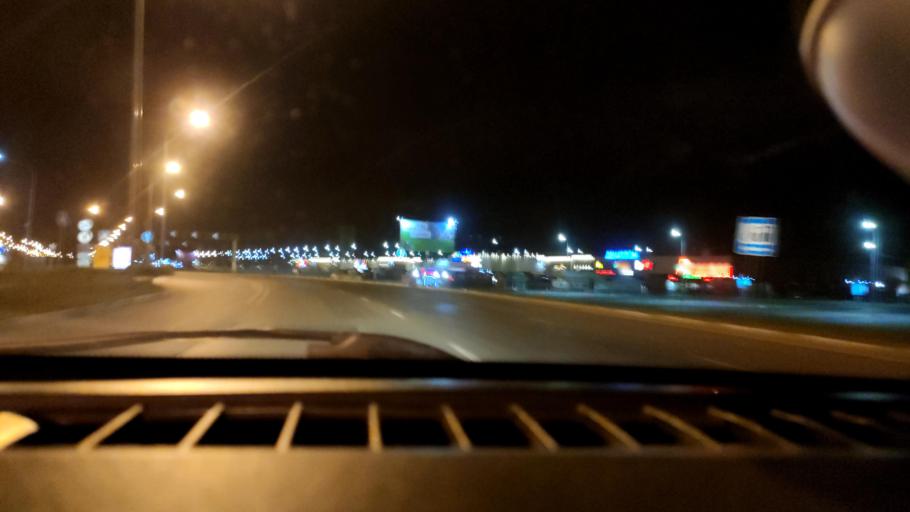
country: RU
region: Samara
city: Samara
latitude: 53.1431
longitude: 50.1798
